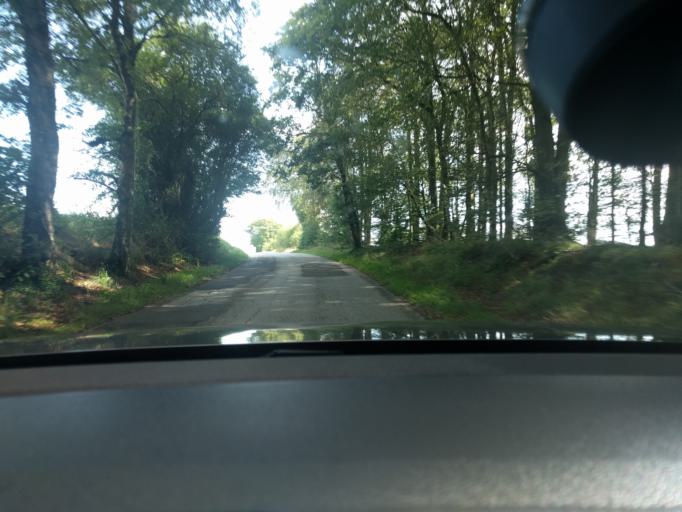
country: DK
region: Central Jutland
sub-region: Viborg Kommune
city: Viborg
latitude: 56.4947
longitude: 9.2888
